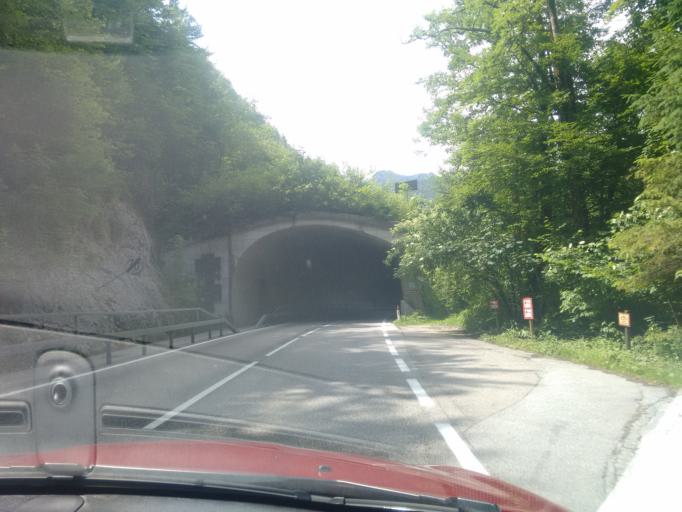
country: AT
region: Upper Austria
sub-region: Politischer Bezirk Gmunden
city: Bad Goisern
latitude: 47.5461
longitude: 13.6591
